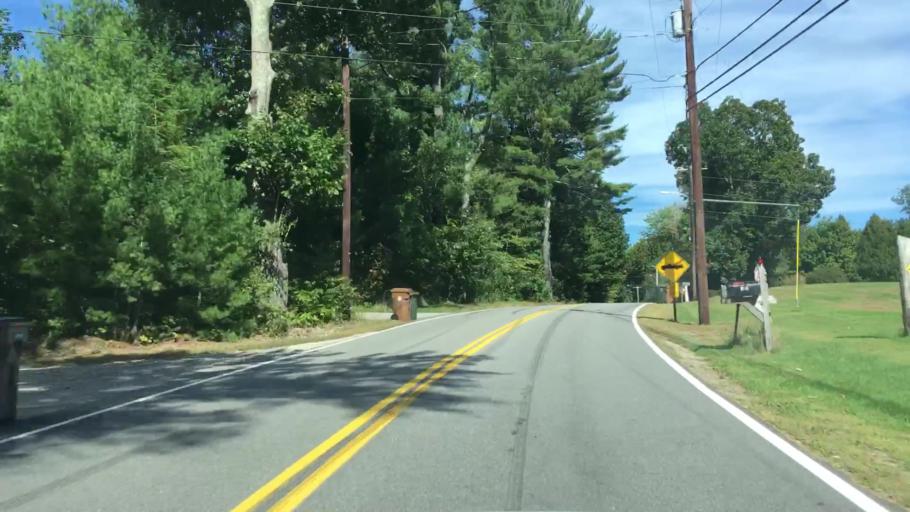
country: US
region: Maine
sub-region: York County
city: Saco
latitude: 43.5686
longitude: -70.4822
